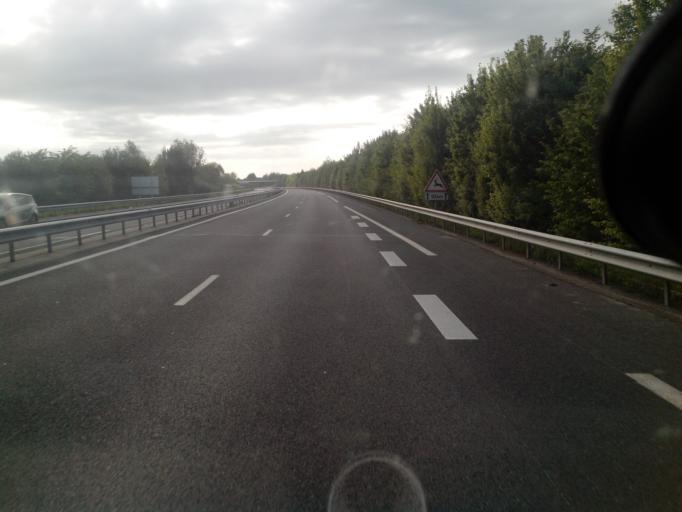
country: FR
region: Haute-Normandie
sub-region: Departement de l'Eure
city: Beuzeville
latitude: 49.3249
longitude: 0.2993
